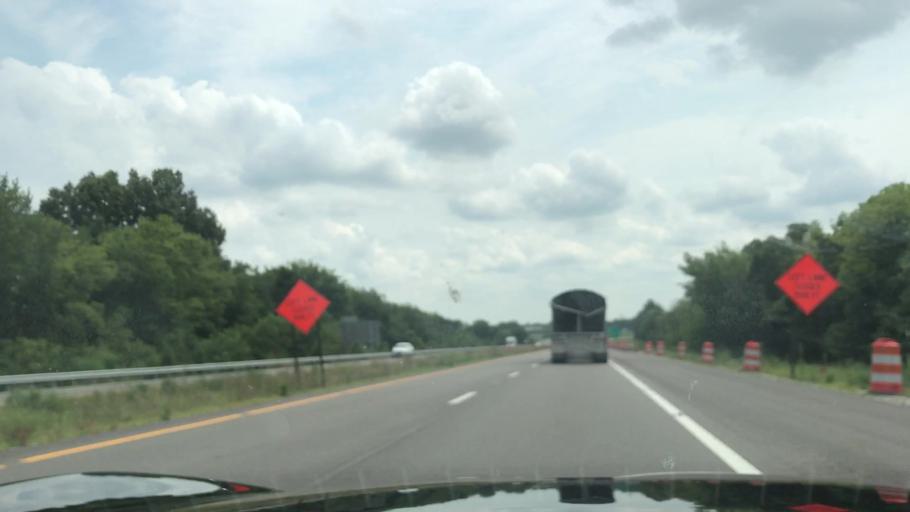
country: US
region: Kentucky
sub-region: Warren County
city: Bowling Green
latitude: 36.9661
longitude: -86.4989
